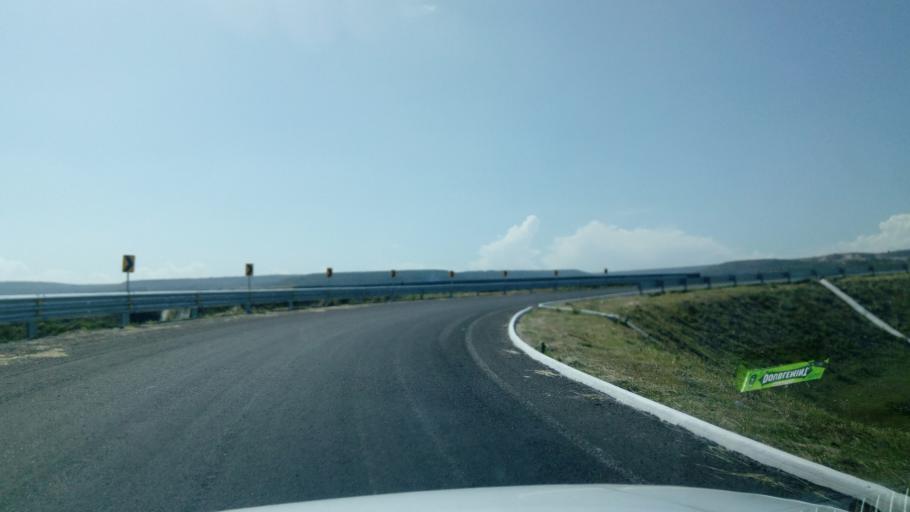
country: MX
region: Durango
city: Victoria de Durango
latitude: 23.9745
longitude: -104.6920
